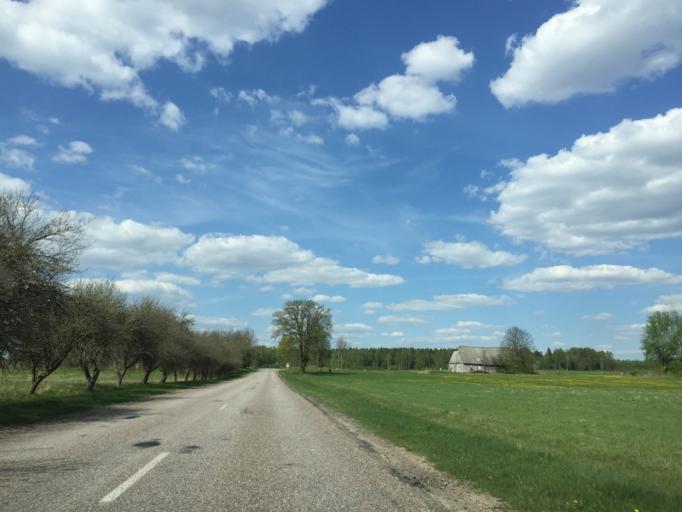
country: LV
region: Limbazu Rajons
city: Limbazi
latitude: 57.3979
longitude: 24.6907
